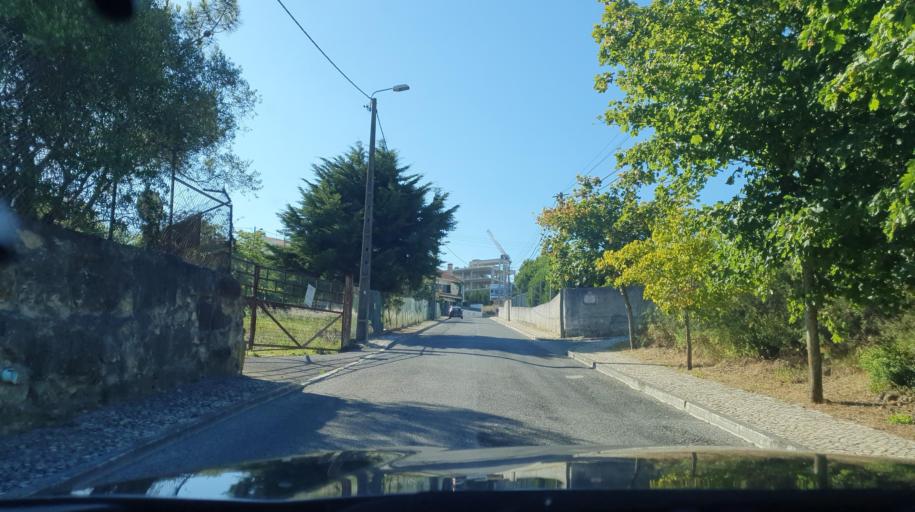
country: PT
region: Lisbon
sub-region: Sintra
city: Belas
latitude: 38.7984
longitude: -9.2525
